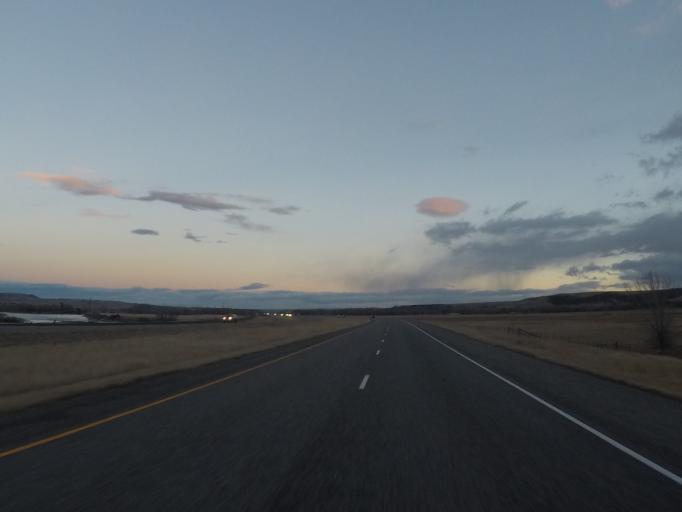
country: US
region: Montana
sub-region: Sweet Grass County
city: Big Timber
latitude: 45.8027
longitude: -109.8518
